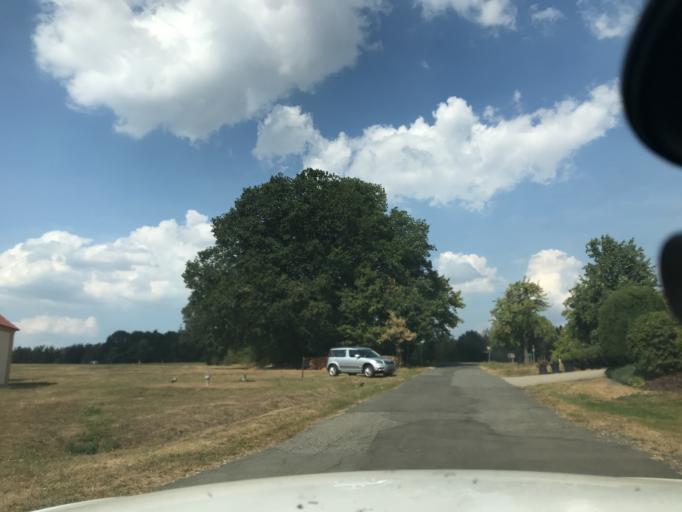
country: DE
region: Bavaria
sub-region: Upper Palatinate
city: Kirchenthumbach
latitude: 49.7656
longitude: 11.6774
